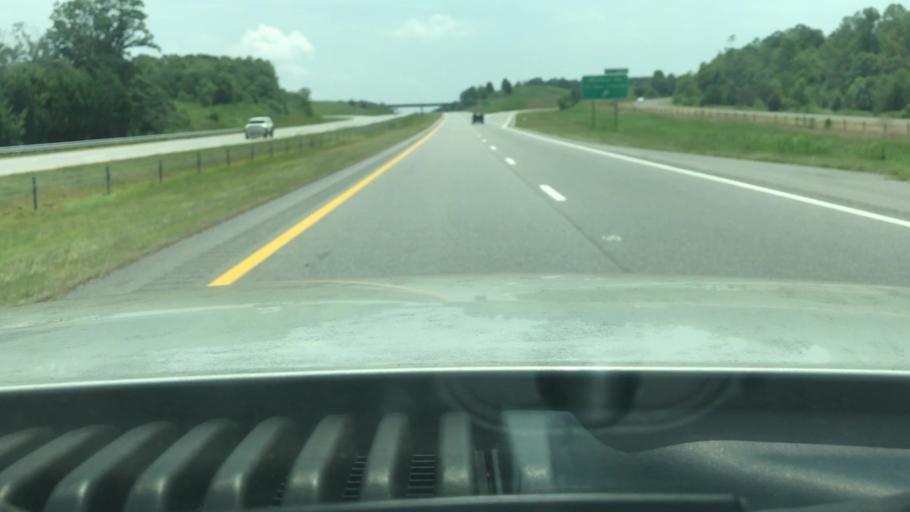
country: US
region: North Carolina
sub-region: Yadkin County
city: Jonesville
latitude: 36.1329
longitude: -80.8494
